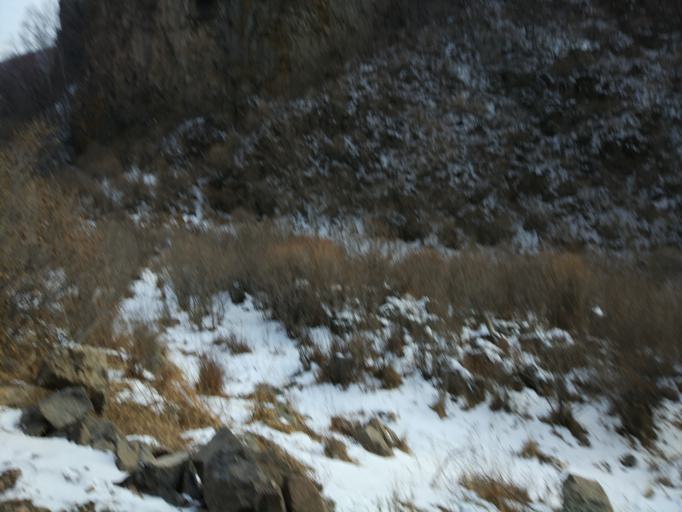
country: CN
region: Hebei
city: Xiwanzi
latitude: 40.8412
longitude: 115.4591
